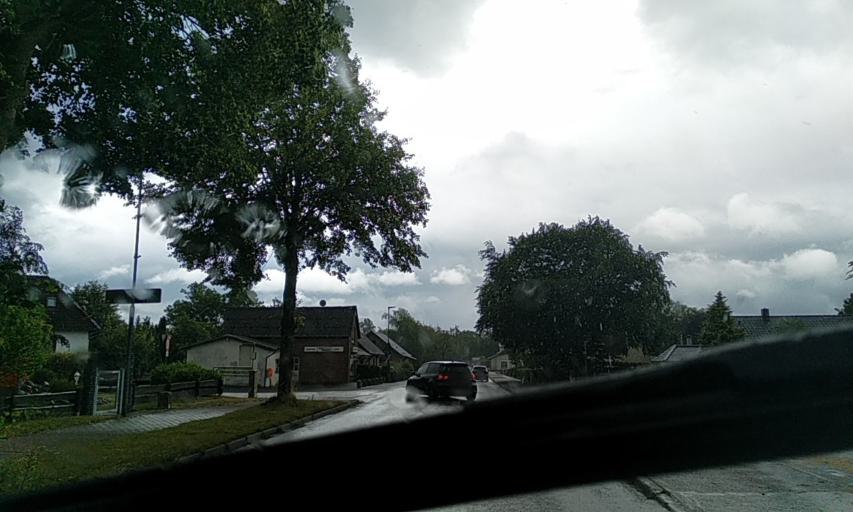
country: DE
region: Schleswig-Holstein
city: Lurschau
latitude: 54.5437
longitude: 9.4955
